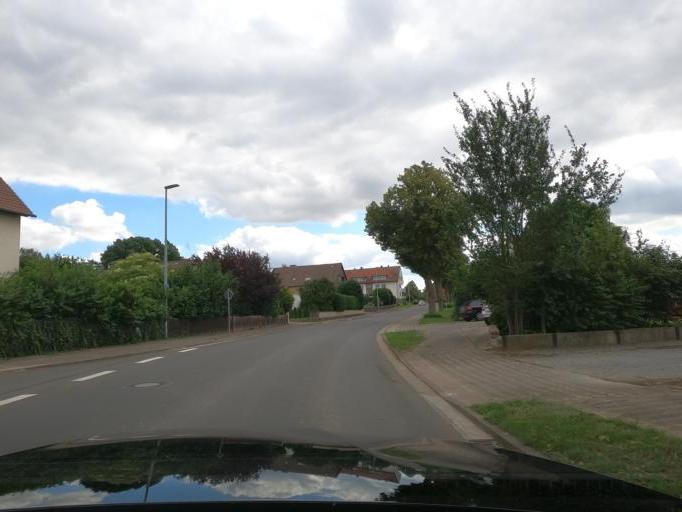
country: DE
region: Lower Saxony
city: Ilsede
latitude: 52.2505
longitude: 10.1597
